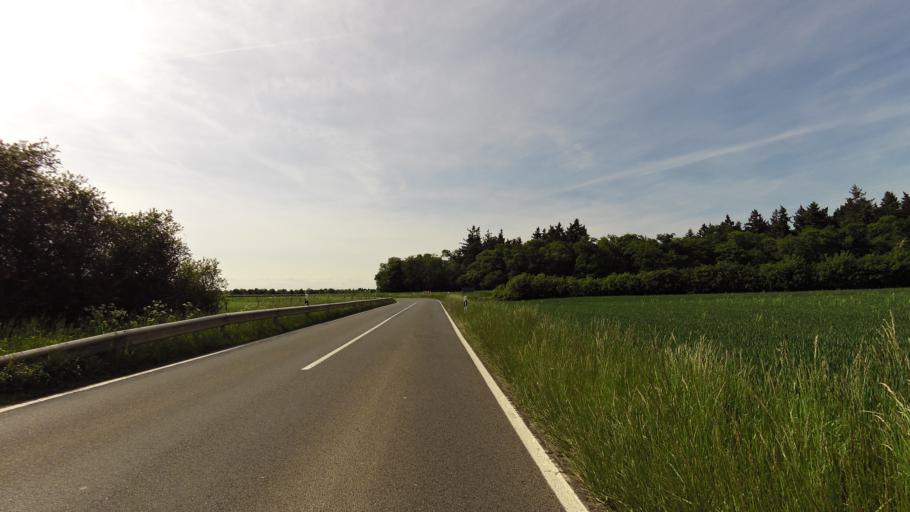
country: DE
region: North Rhine-Westphalia
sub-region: Regierungsbezirk Koln
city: Rheinbach
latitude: 50.6645
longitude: 6.9694
